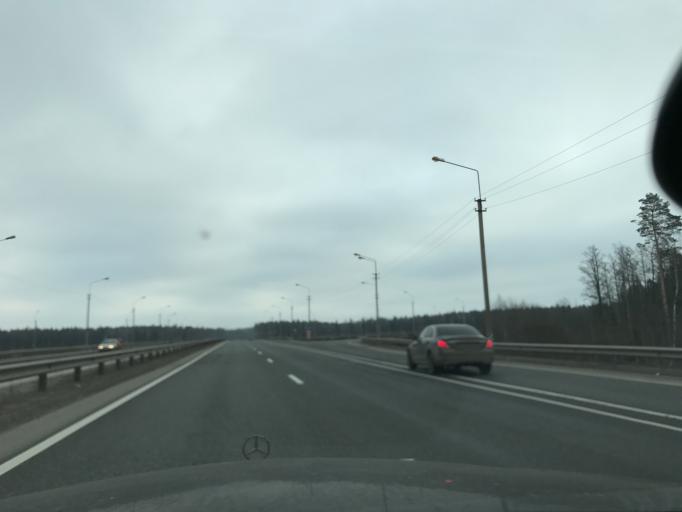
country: RU
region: Vladimir
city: Kommunar
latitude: 56.0767
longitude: 40.4701
